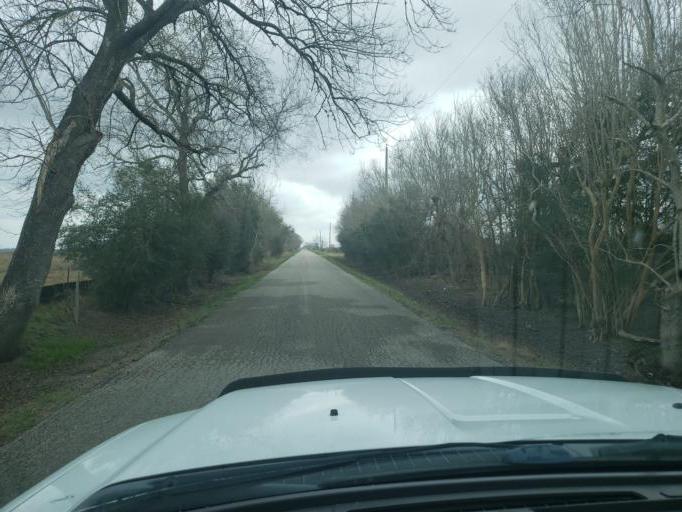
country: US
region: Texas
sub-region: Fort Bend County
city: Needville
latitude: 29.3460
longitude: -95.7584
